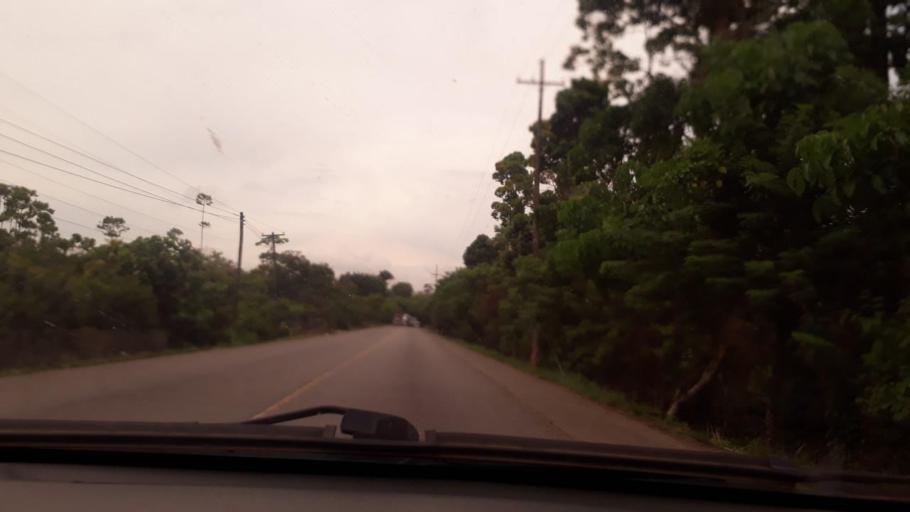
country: GT
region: Izabal
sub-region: Municipio de Puerto Barrios
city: Puerto Barrios
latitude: 15.6259
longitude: -88.5569
